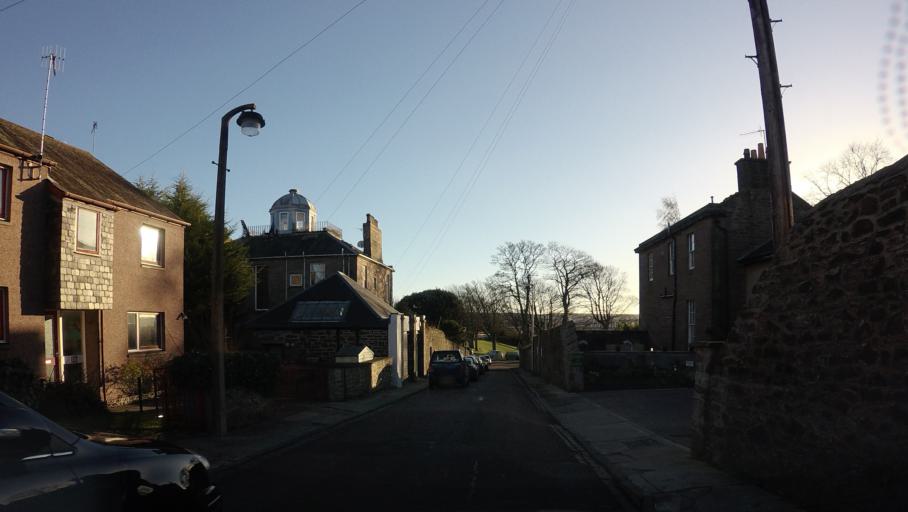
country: GB
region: Scotland
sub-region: Dundee City
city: Dundee
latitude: 56.4538
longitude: -2.9894
